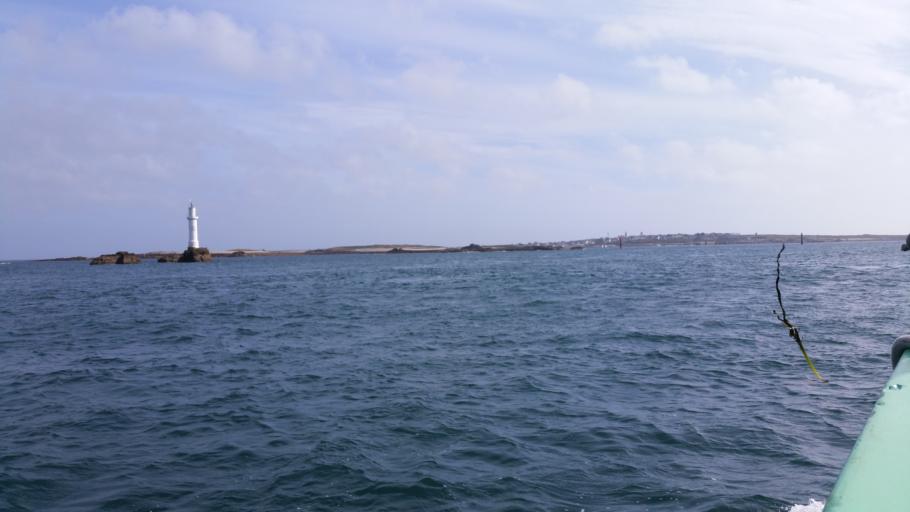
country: FR
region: Brittany
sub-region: Departement du Finistere
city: Le Conquet
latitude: 48.4140
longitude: -4.9479
